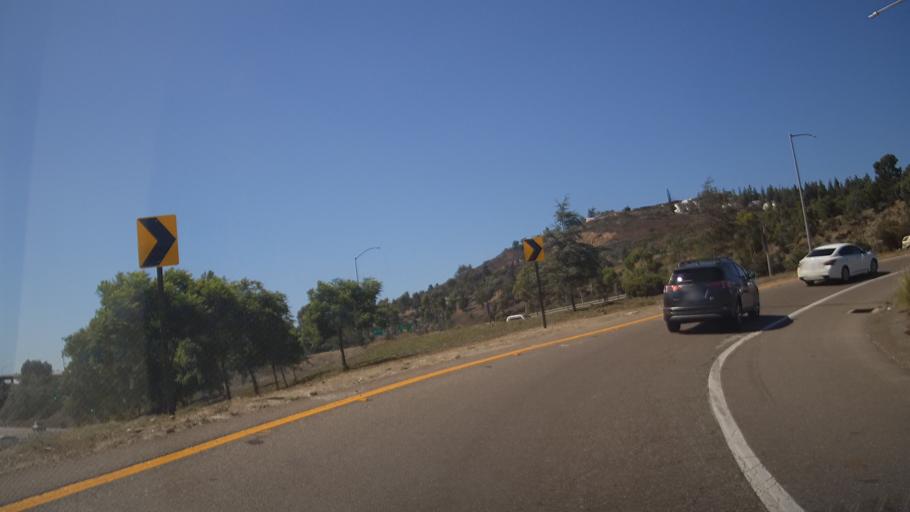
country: US
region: California
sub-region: San Diego County
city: Spring Valley
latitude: 32.7519
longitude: -117.0115
